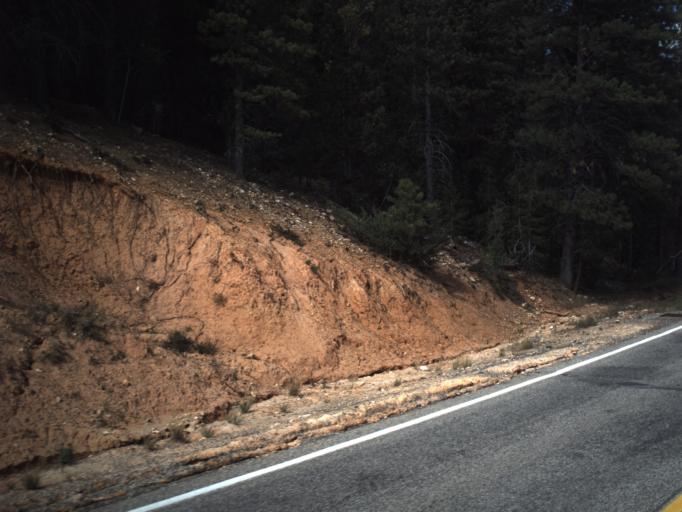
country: US
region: Utah
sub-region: Garfield County
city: Panguitch
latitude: 37.4942
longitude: -112.6067
